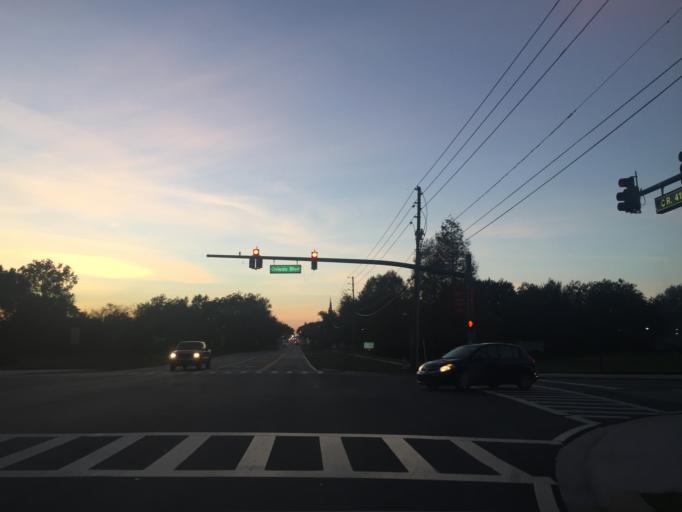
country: US
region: Florida
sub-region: Seminole County
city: Oviedo
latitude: 28.6703
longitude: -81.2040
